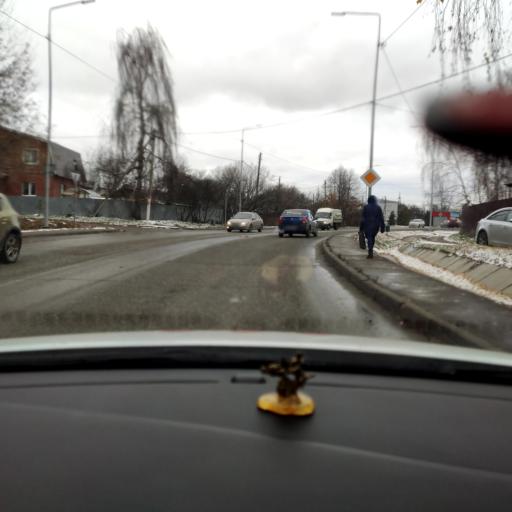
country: RU
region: Tatarstan
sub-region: Zelenodol'skiy Rayon
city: Zelenodolsk
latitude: 55.8473
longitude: 48.5477
